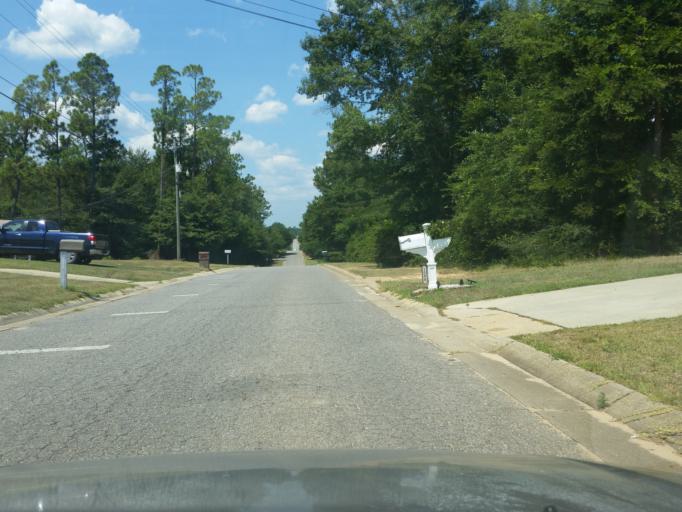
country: US
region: Florida
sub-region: Escambia County
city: Cantonment
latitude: 30.6429
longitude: -87.2964
